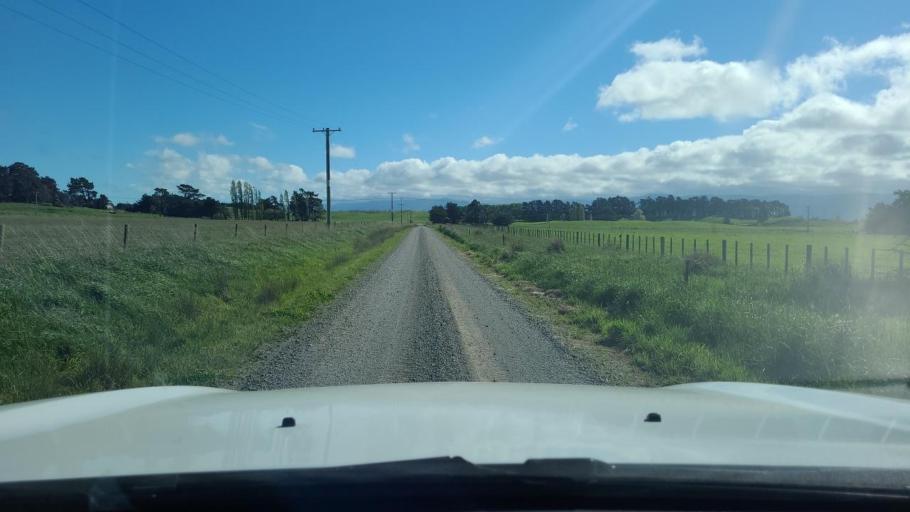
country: NZ
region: Wellington
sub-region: South Wairarapa District
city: Waipawa
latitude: -41.2004
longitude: 175.3605
